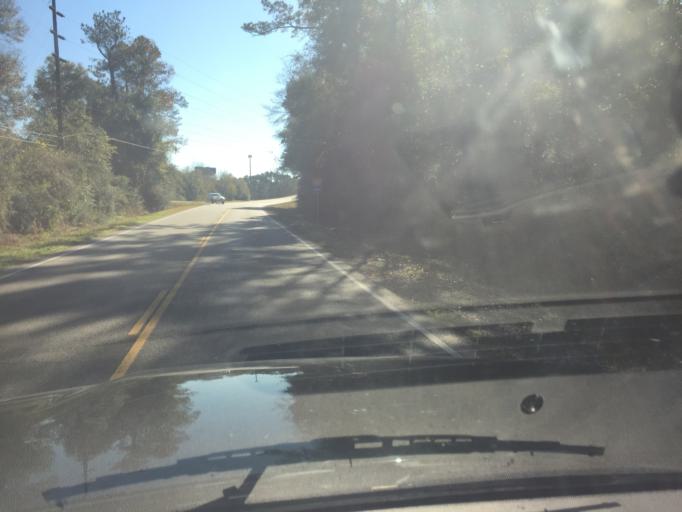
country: US
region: Louisiana
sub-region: Saint Tammany Parish
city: Slidell
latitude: 30.3049
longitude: -89.7264
